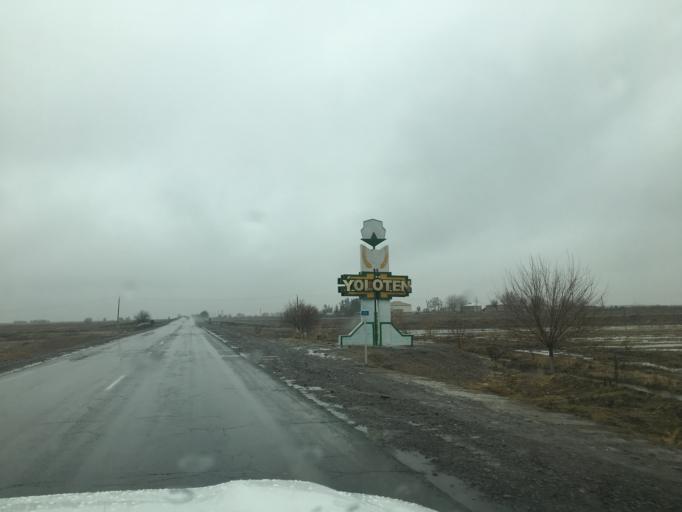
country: TM
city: Murgab
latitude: 37.4462
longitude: 62.0837
